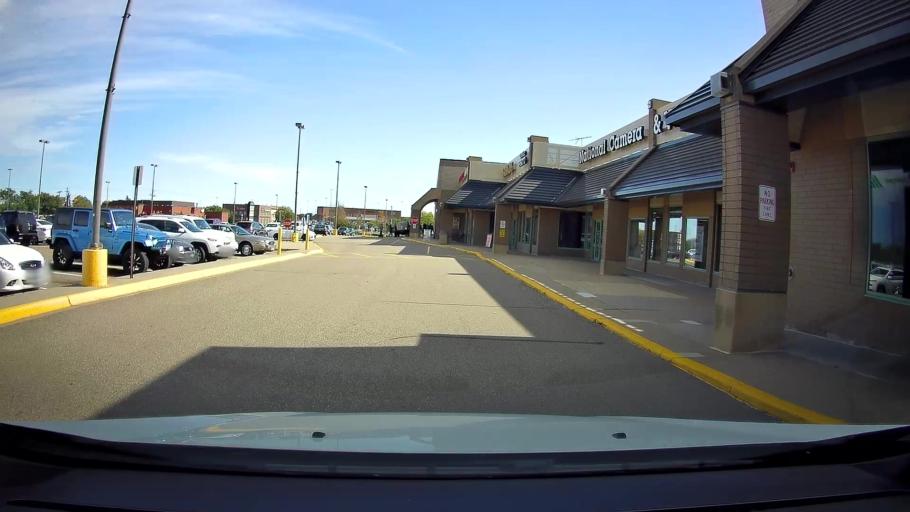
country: US
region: Minnesota
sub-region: Ramsey County
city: Roseville
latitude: 45.0131
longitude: -93.1791
